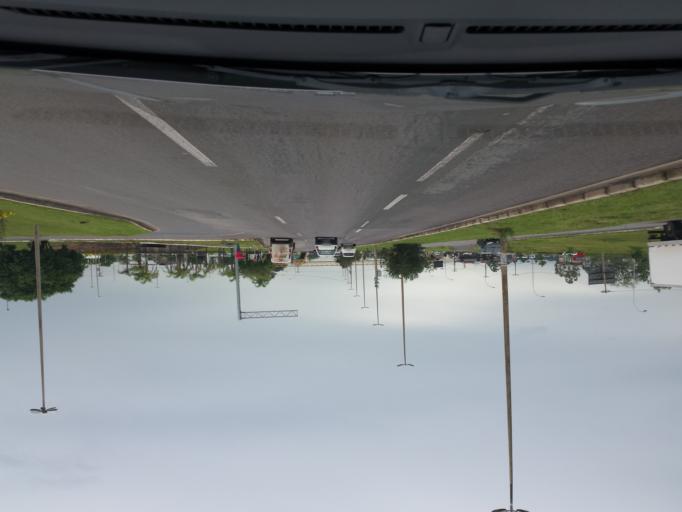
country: BR
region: Federal District
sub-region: Brasilia
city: Brasilia
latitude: -15.8610
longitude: -47.9565
